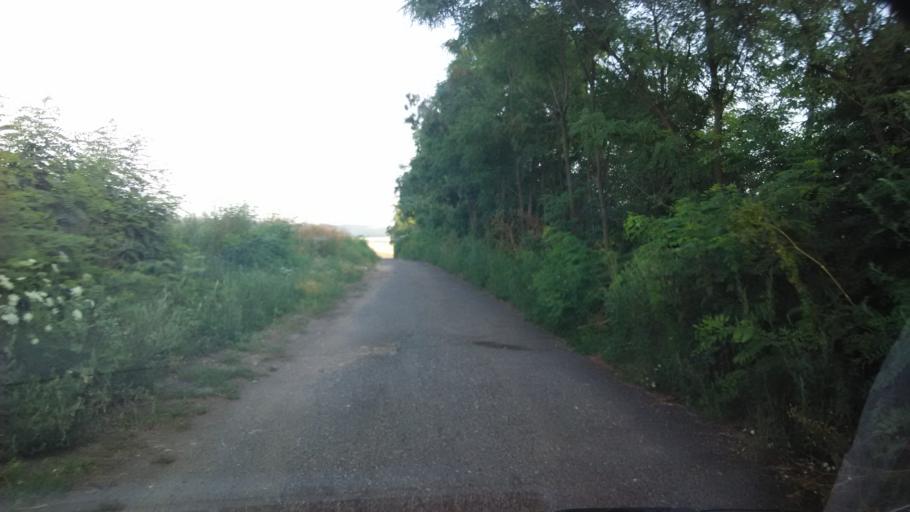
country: SK
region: Nitriansky
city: Levice
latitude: 48.2802
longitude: 18.7184
